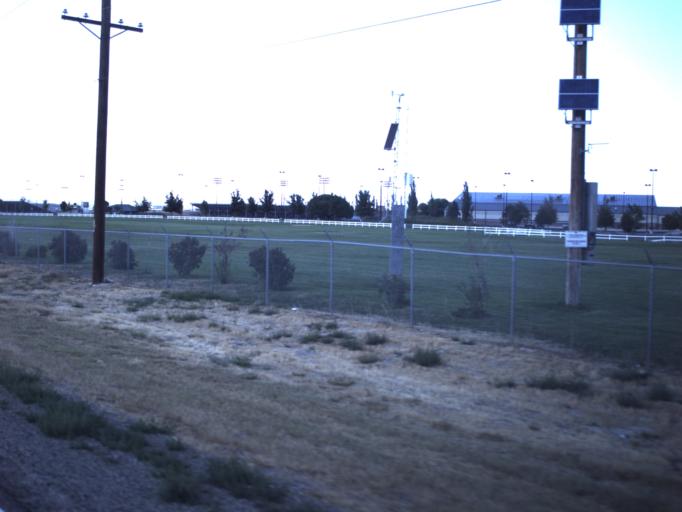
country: US
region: Utah
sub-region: Tooele County
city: Erda
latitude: 40.5685
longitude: -112.3710
